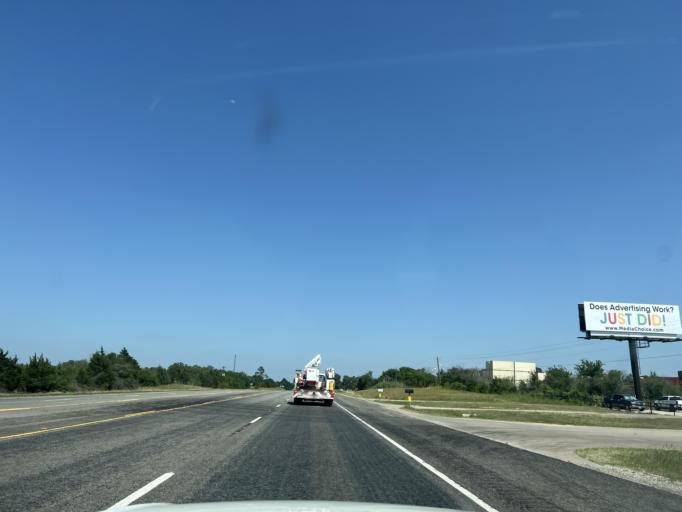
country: US
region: Texas
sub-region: Washington County
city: Brenham
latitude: 30.1729
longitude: -96.4512
